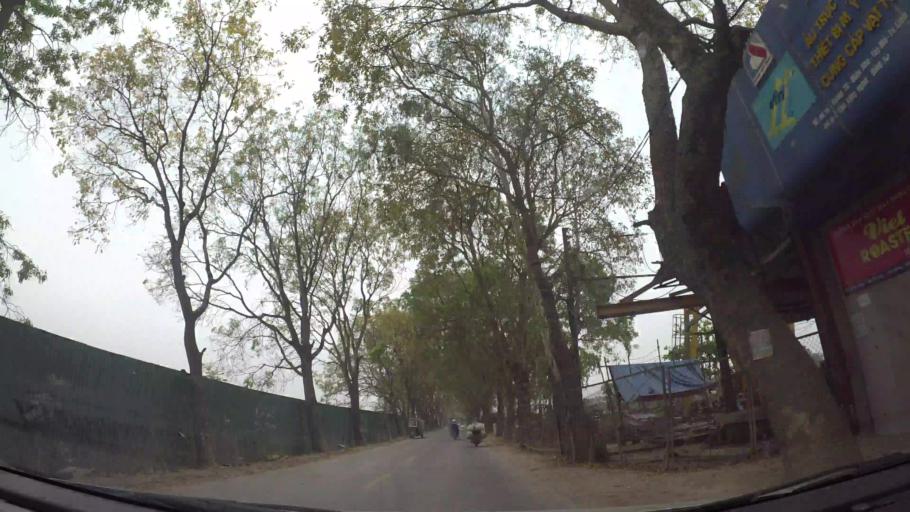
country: VN
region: Ha Noi
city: Cau Dien
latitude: 21.0205
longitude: 105.7436
